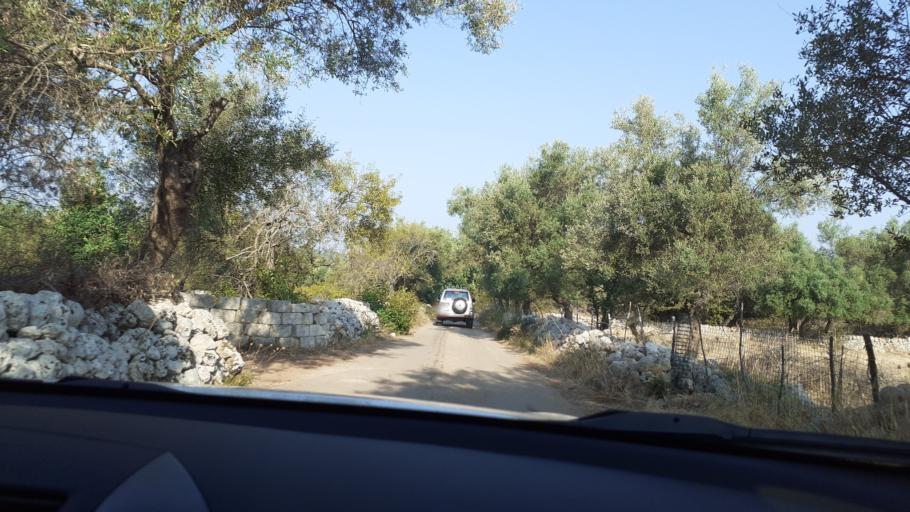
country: IT
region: Sicily
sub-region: Provincia di Siracusa
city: Cassibile
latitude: 36.9810
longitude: 15.1429
